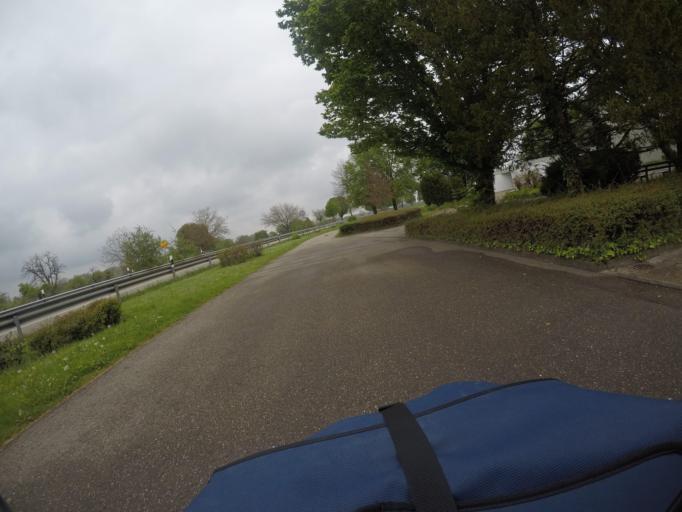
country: DE
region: Baden-Wuerttemberg
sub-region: Karlsruhe Region
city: Iffezheim
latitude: 48.8496
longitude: 8.1408
